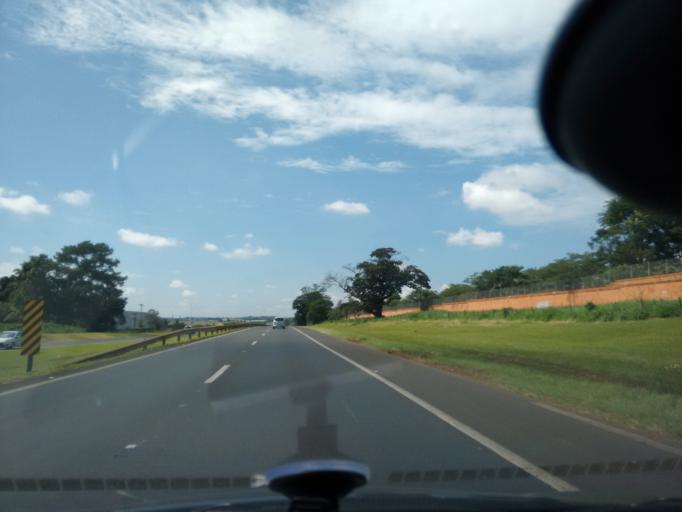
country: BR
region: Sao Paulo
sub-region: Sao Carlos
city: Sao Carlos
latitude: -21.9779
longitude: -47.9281
